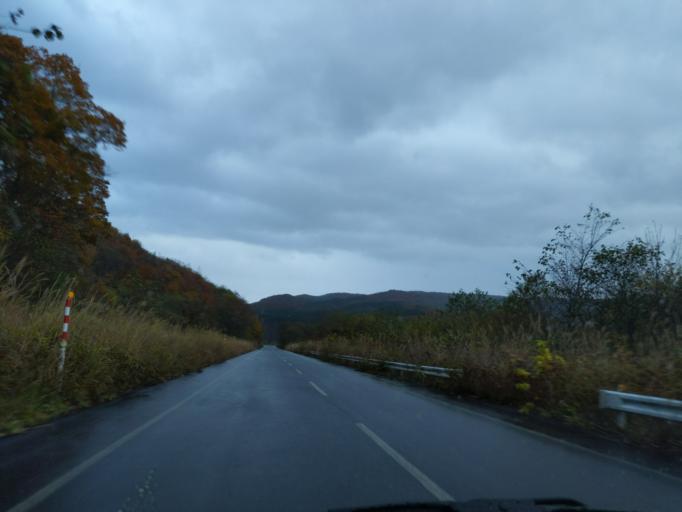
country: JP
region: Iwate
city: Ichinoseki
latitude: 39.0196
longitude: 140.8759
